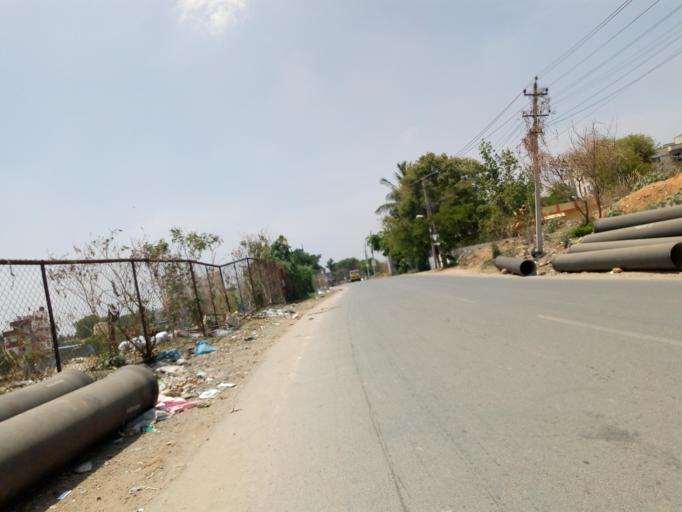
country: IN
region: Karnataka
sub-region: Bangalore Urban
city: Bangalore
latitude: 12.8844
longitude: 77.6559
